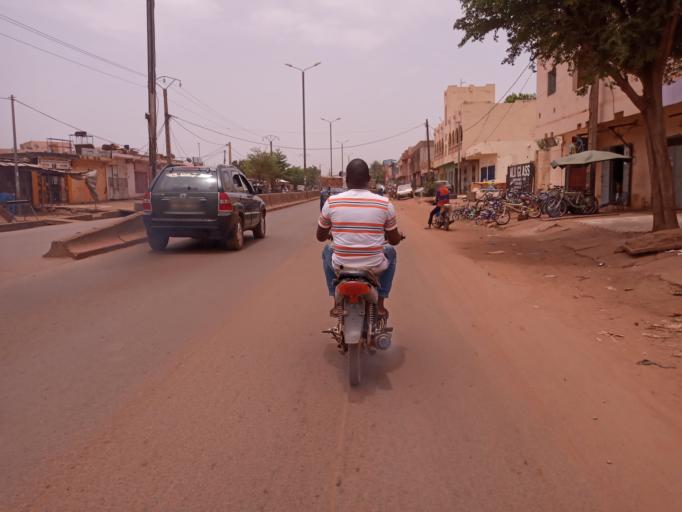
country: ML
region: Bamako
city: Bamako
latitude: 12.5948
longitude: -8.0171
